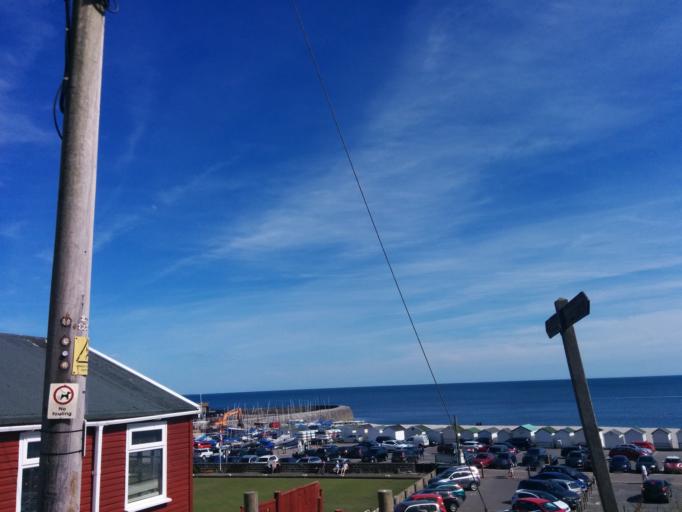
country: GB
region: England
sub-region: Dorset
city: Lyme Regis
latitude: 50.7208
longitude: -2.9412
